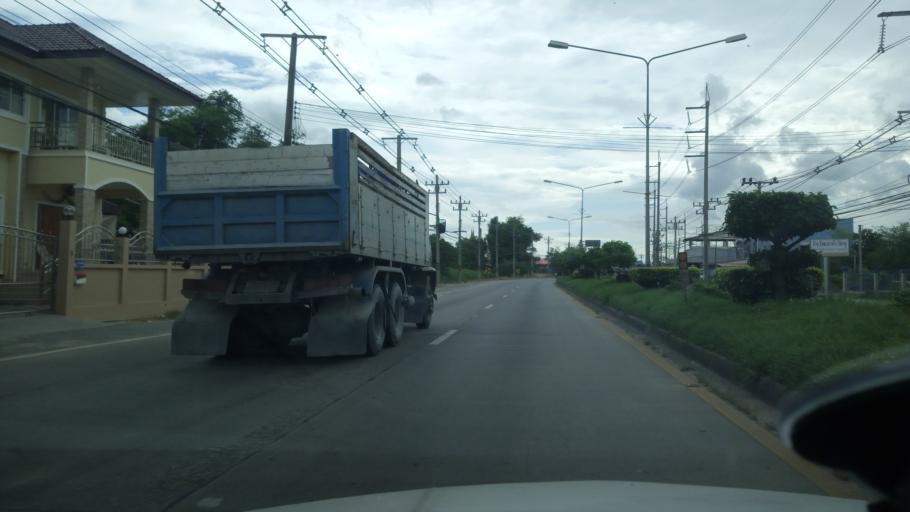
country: TH
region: Chon Buri
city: Phanat Nikhom
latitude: 13.4453
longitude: 101.1632
